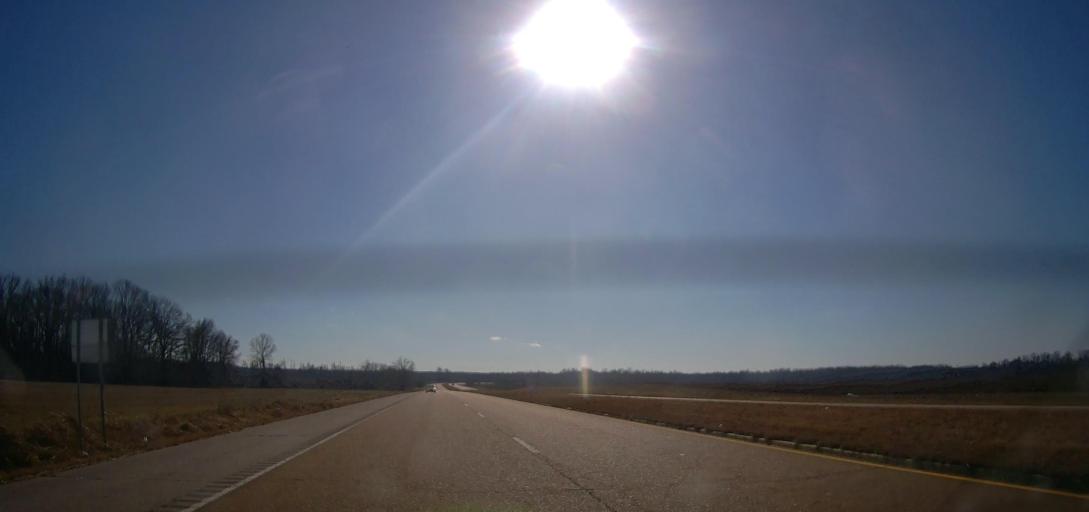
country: US
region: Tennessee
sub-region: Shelby County
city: Millington
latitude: 35.2945
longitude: -89.8821
